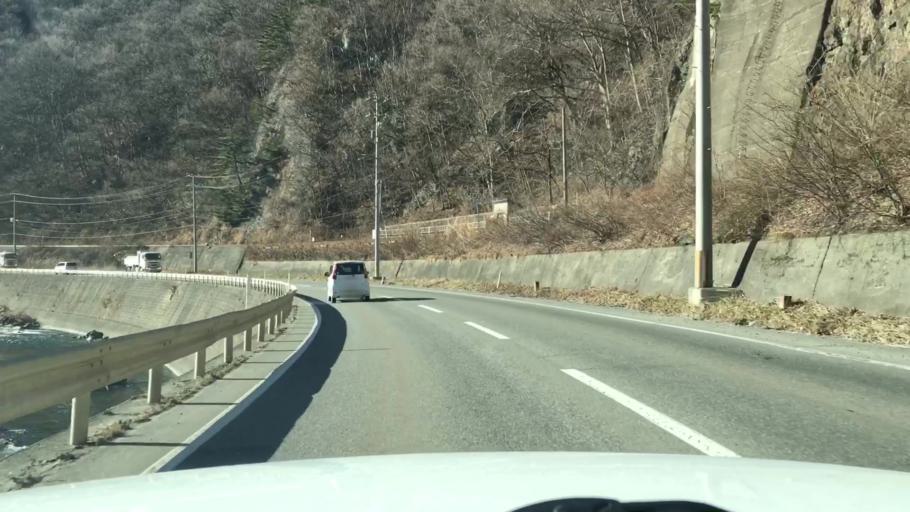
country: JP
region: Iwate
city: Miyako
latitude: 39.6109
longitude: 141.7760
